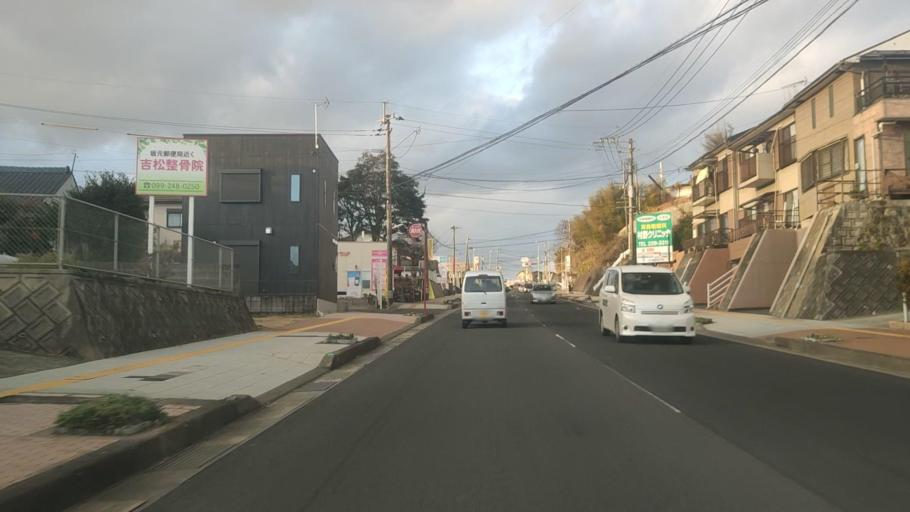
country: JP
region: Kagoshima
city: Kagoshima-shi
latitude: 31.6189
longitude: 130.5537
